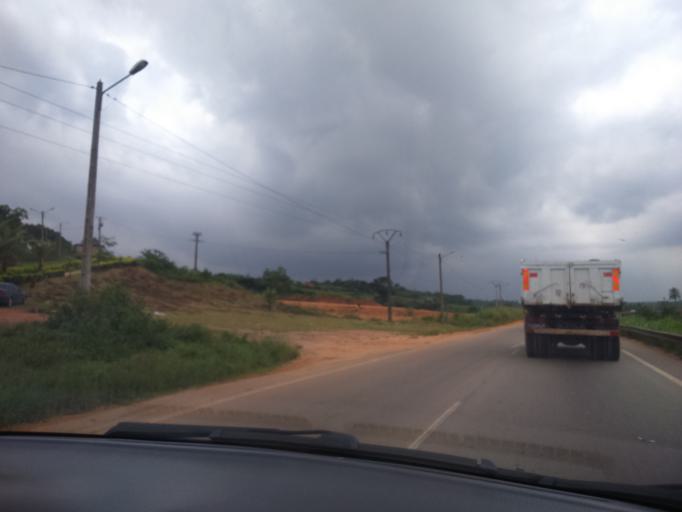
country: CI
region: Lagunes
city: Anyama
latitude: 5.5089
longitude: -4.0617
